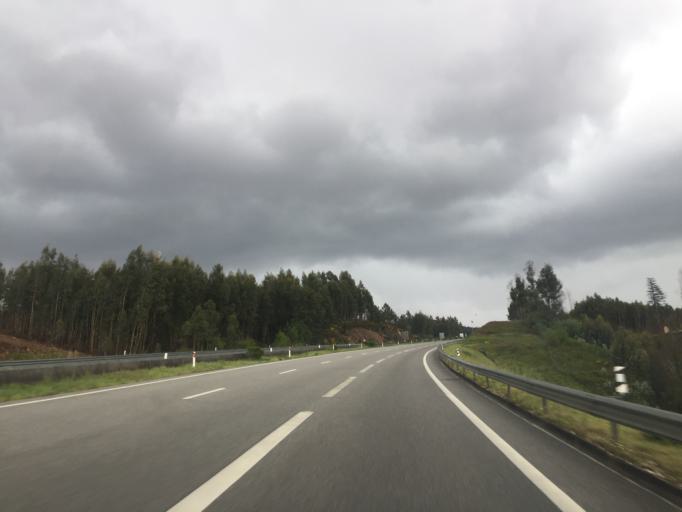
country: PT
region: Aveiro
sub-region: Agueda
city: Valongo
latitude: 40.6655
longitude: -8.3980
